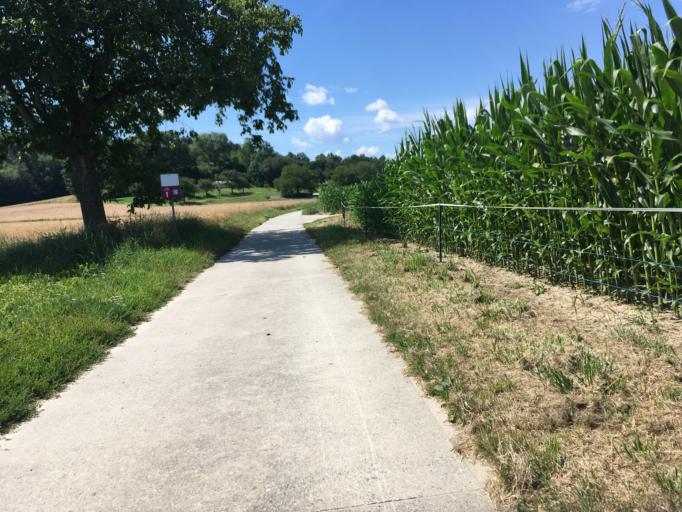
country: CH
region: Fribourg
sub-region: Broye District
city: Domdidier
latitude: 46.9314
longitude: 6.9887
